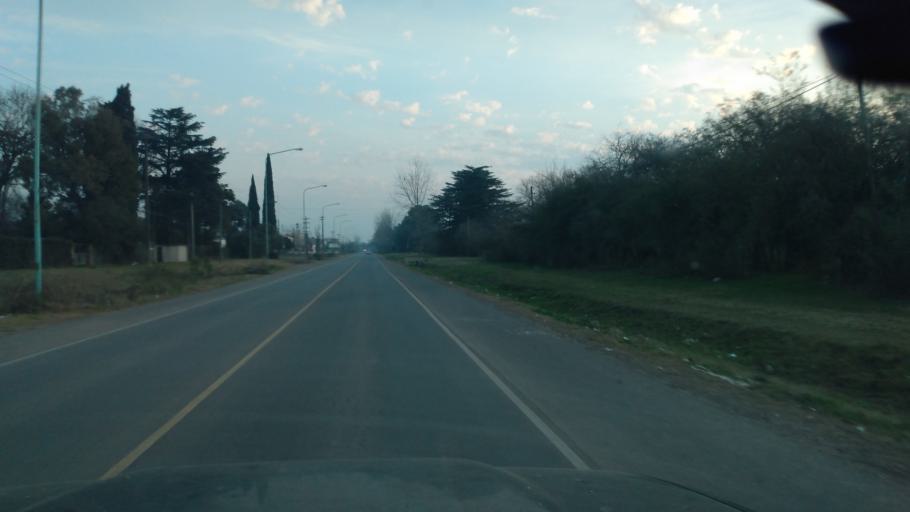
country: AR
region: Buenos Aires
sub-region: Partido de Lujan
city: Lujan
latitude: -34.5590
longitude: -59.1314
